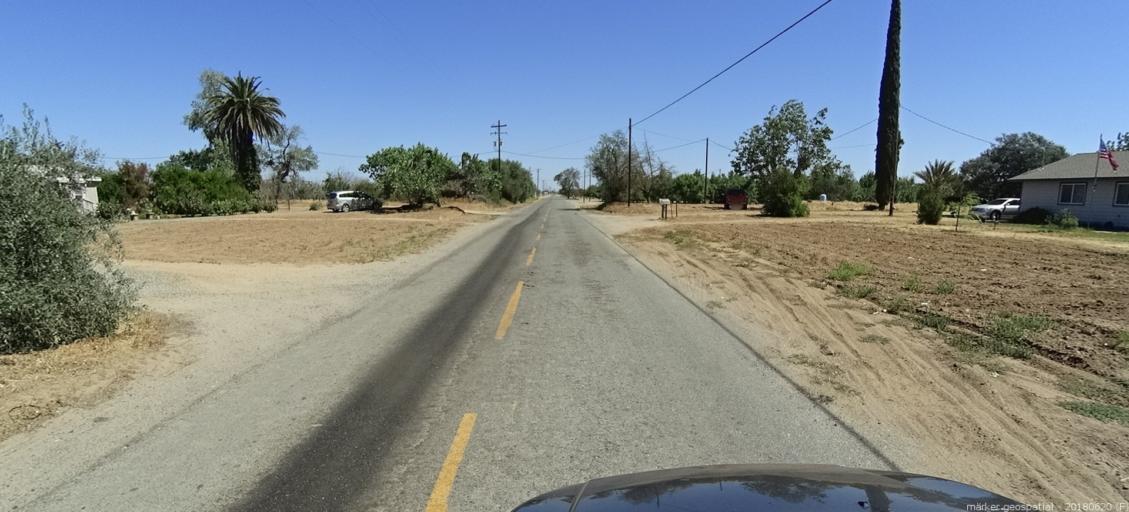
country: US
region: California
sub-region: Madera County
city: Parkwood
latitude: 36.8853
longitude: -120.0105
